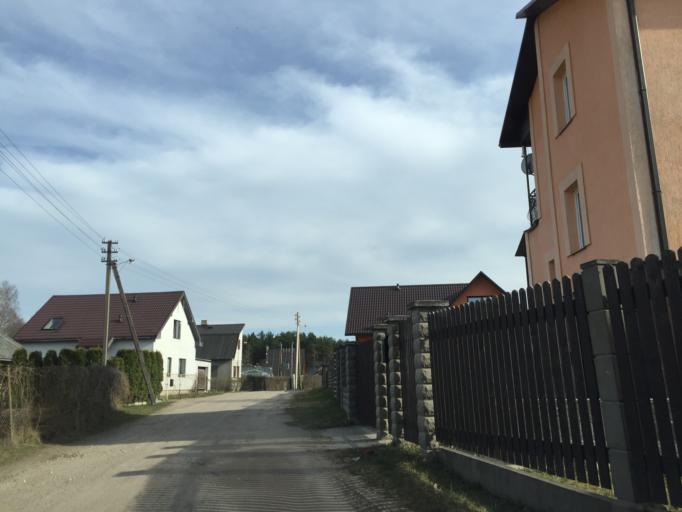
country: LV
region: Ogre
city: Ogre
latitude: 56.8069
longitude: 24.6390
